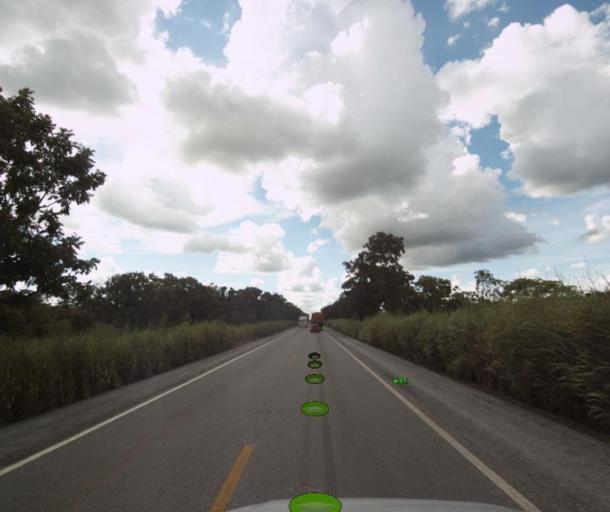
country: BR
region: Goias
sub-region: Porangatu
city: Porangatu
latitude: -13.1792
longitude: -49.1687
